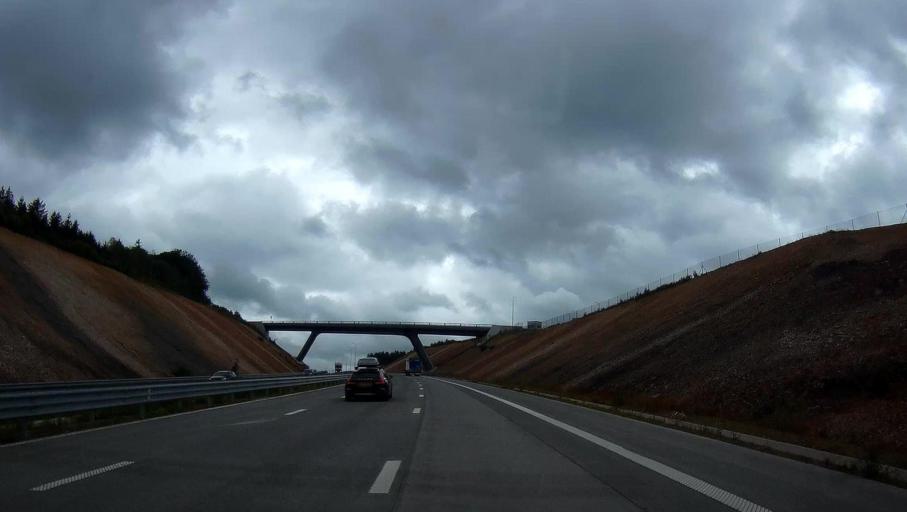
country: BE
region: Wallonia
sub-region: Province de Namur
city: Couvin
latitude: 50.0298
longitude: 4.5112
